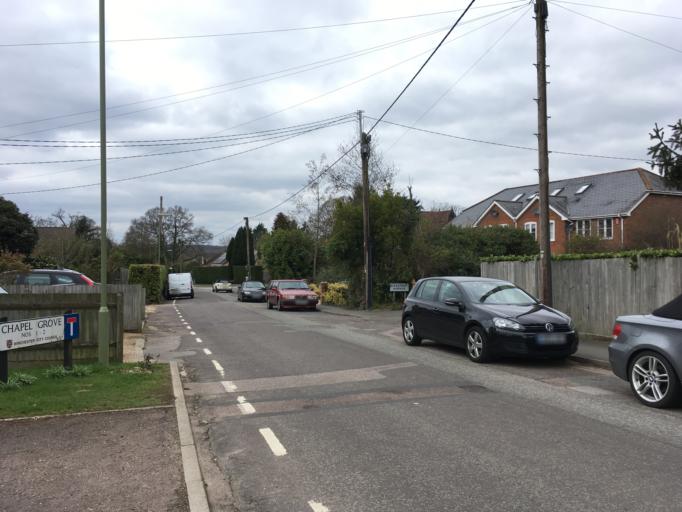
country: GB
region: England
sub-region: Hampshire
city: Colden Common
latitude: 50.9974
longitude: -1.3192
